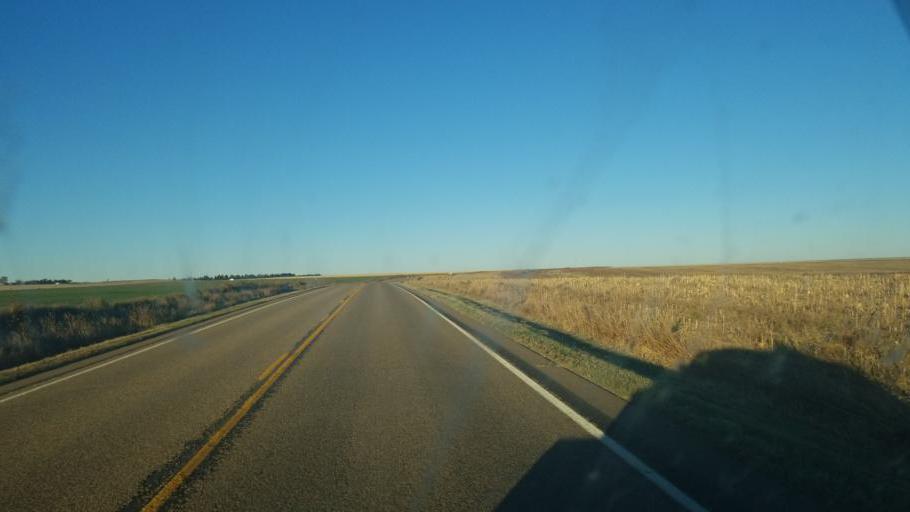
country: US
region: Colorado
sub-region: Cheyenne County
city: Cheyenne Wells
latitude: 38.8089
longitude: -102.4157
